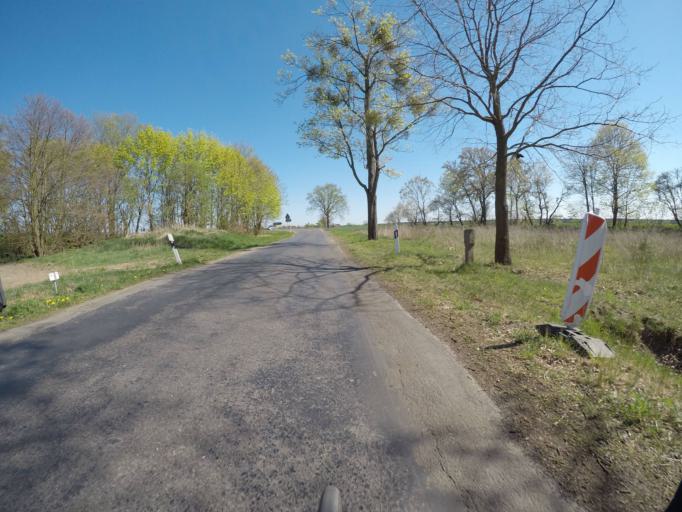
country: DE
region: Brandenburg
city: Strausberg
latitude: 52.6139
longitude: 13.8561
